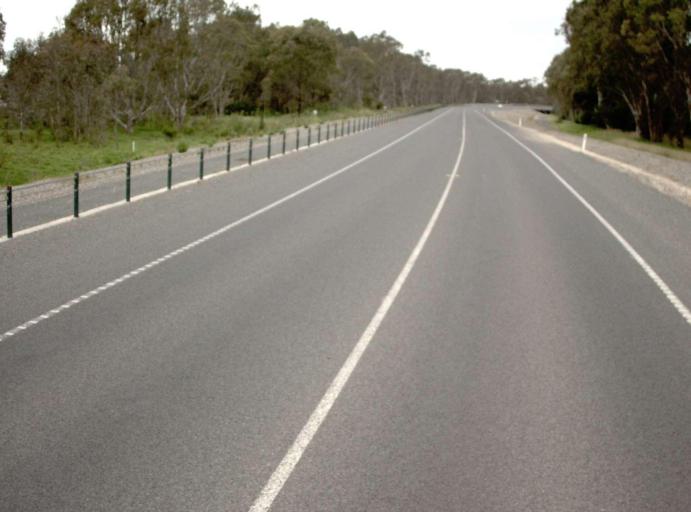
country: AU
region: Victoria
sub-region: Wellington
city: Sale
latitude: -38.1309
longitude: 147.0723
